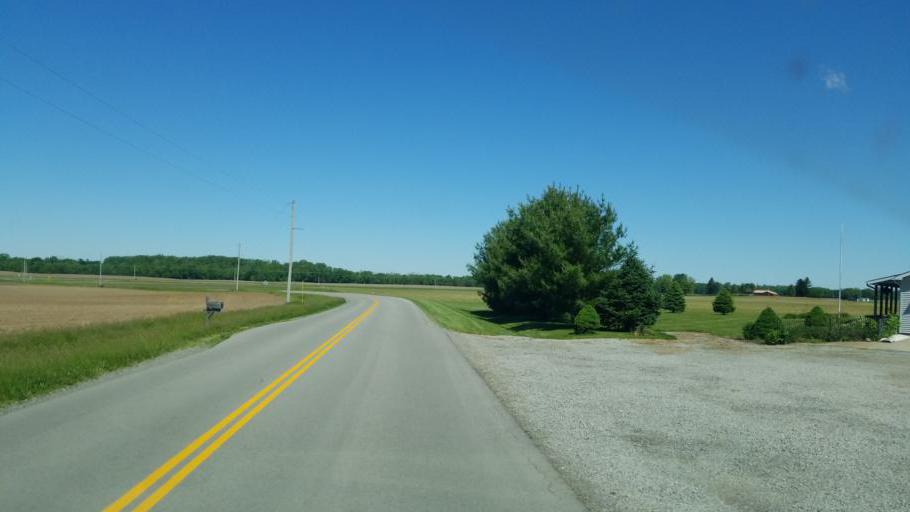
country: US
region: Ohio
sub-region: Logan County
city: Russells Point
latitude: 40.4184
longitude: -83.9030
